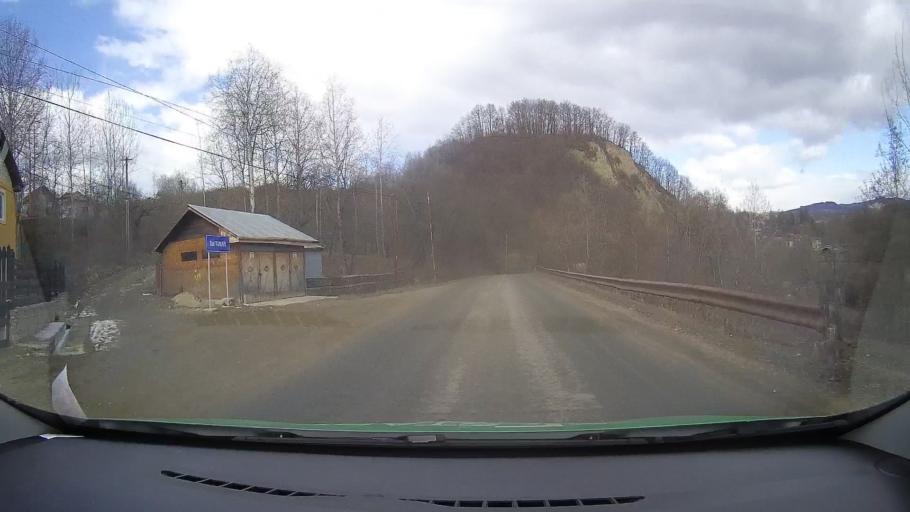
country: RO
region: Dambovita
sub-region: Comuna Buciumeni
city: Buciumeni
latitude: 45.1251
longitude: 25.4669
